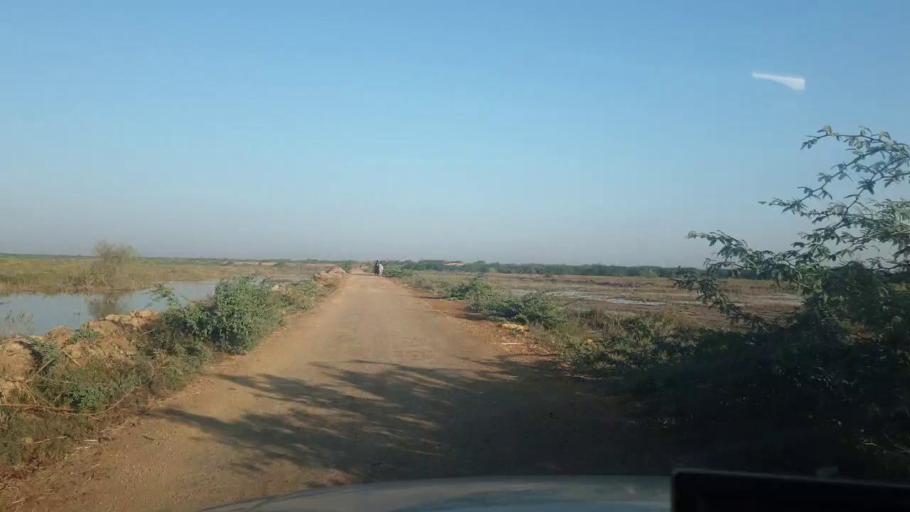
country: PK
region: Sindh
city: Thatta
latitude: 24.7029
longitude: 67.8499
